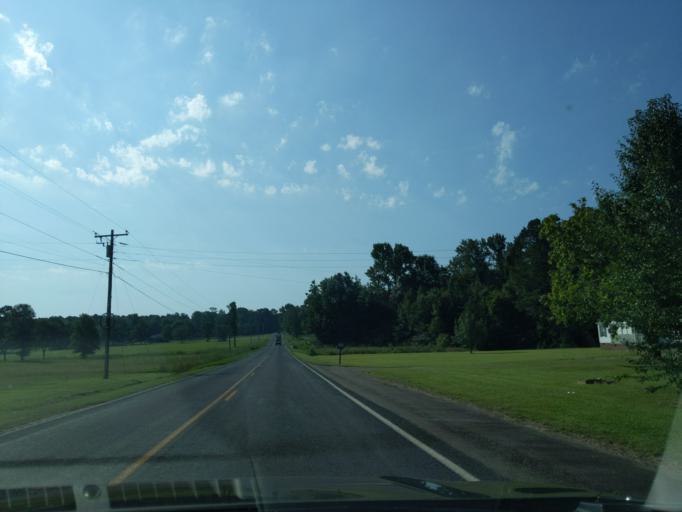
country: US
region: South Carolina
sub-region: Lexington County
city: Leesville
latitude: 34.0250
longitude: -81.5292
